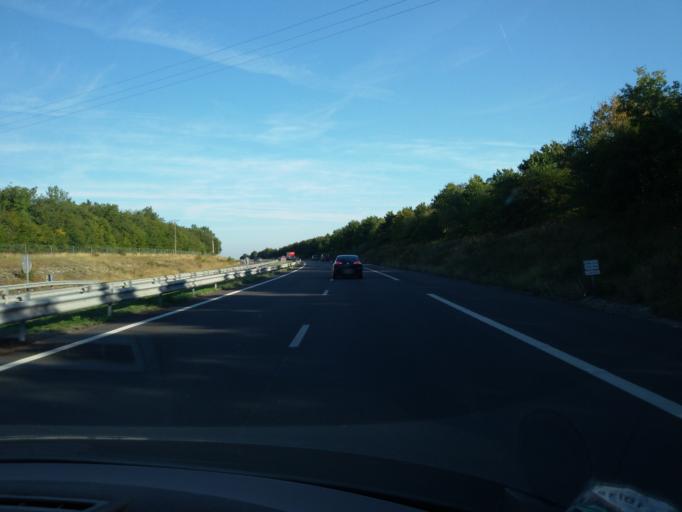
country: FR
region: Centre
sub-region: Departement du Cher
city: Plaimpied-Givaudins
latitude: 46.9764
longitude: 2.4232
